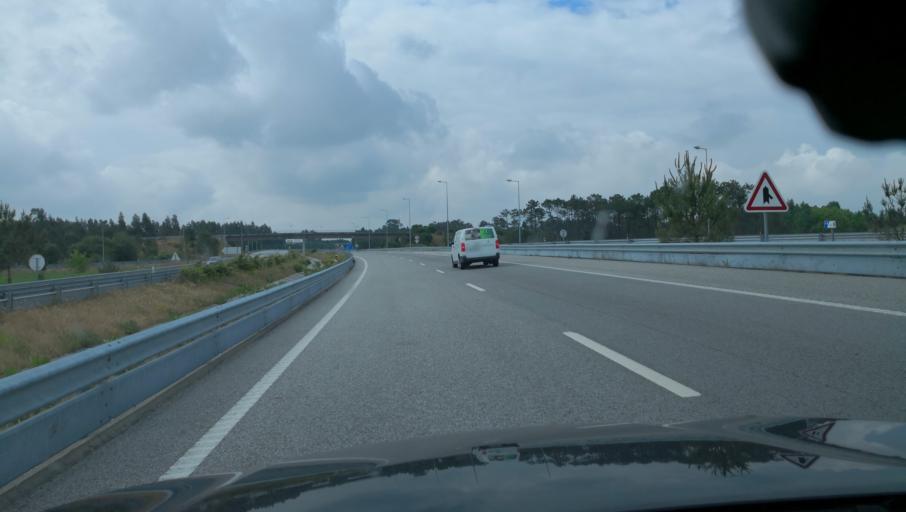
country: PT
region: Coimbra
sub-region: Montemor-O-Velho
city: Arazede
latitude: 40.3263
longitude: -8.7223
